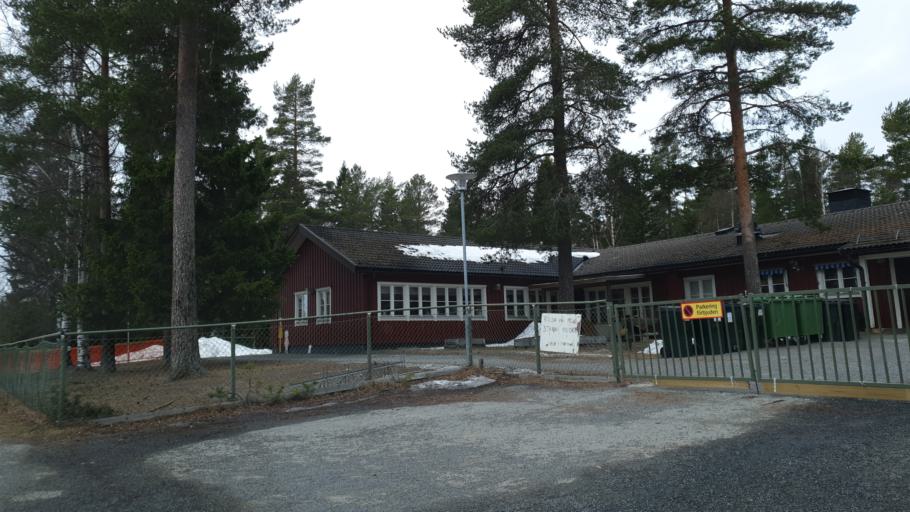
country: SE
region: Vaesterbotten
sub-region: Robertsfors Kommun
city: Robertsfors
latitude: 64.1961
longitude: 20.8537
